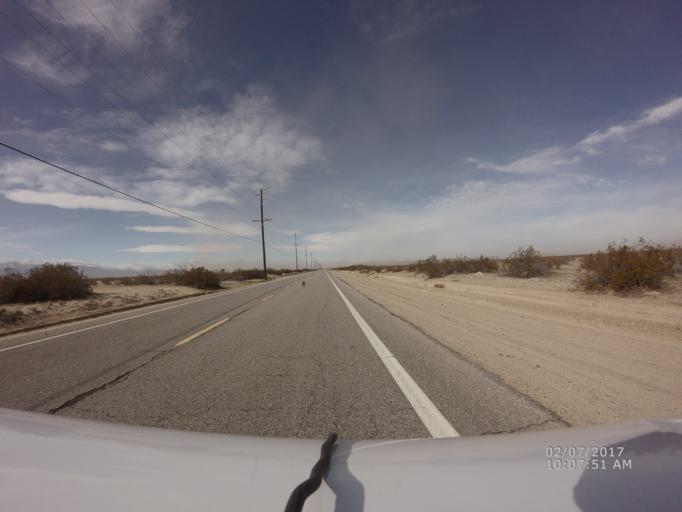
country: US
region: California
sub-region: Los Angeles County
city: Lake Los Angeles
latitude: 34.5799
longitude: -117.7475
